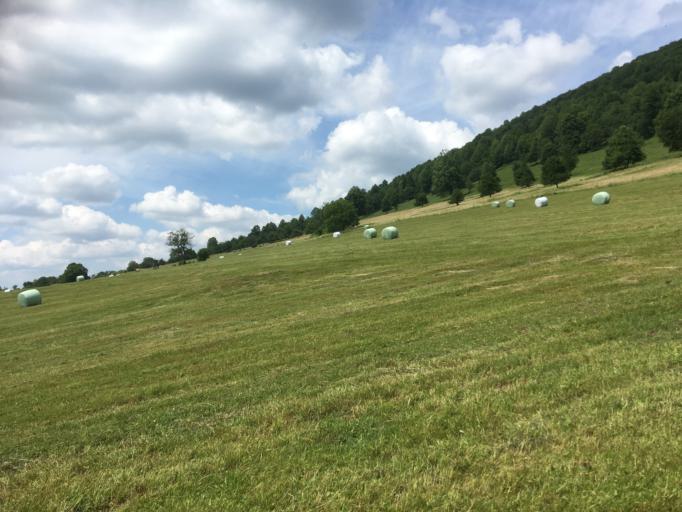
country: SI
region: Kocevje
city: Kocevje
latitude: 45.6106
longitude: 14.9661
